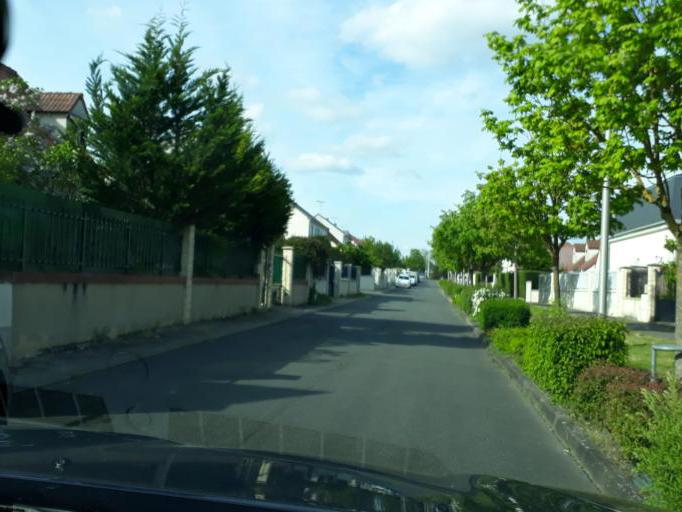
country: FR
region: Centre
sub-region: Departement du Loiret
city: Saran
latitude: 47.9317
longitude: 1.8913
